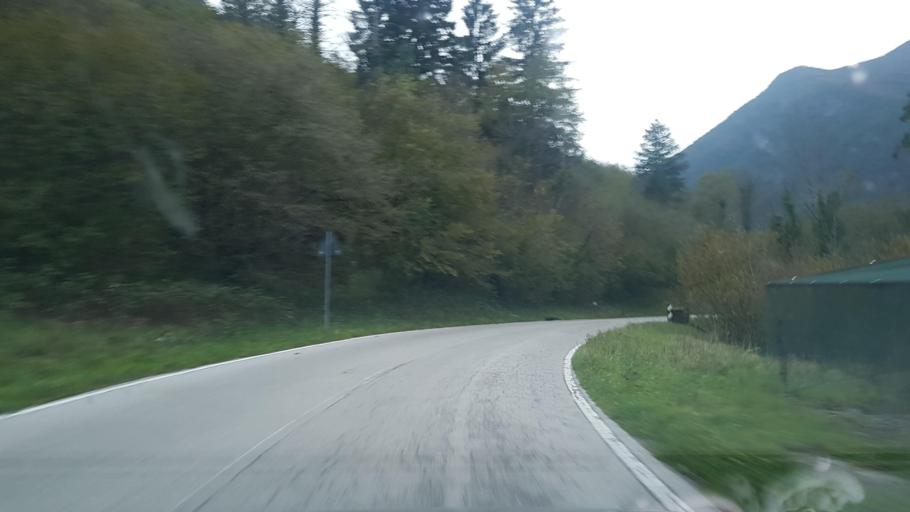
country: IT
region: Friuli Venezia Giulia
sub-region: Provincia di Pordenone
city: Anduins
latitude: 46.3102
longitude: 12.9357
